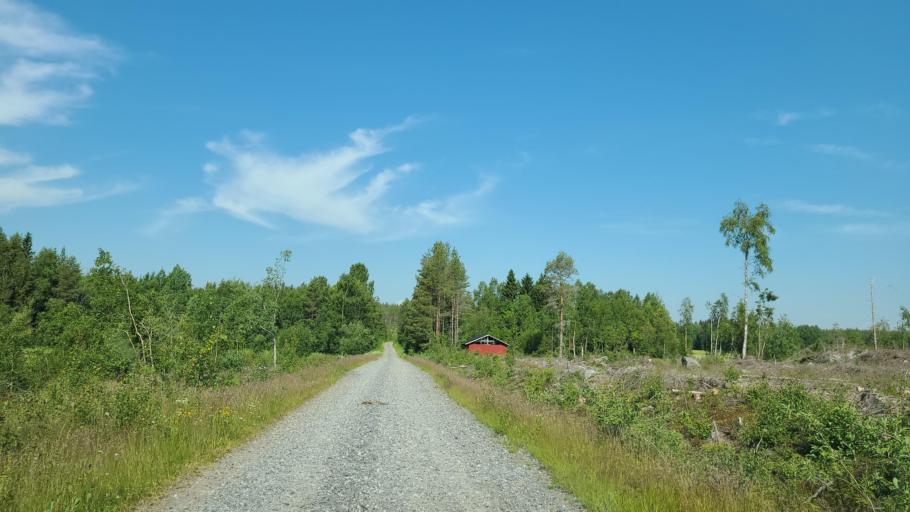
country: SE
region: Vaesterbotten
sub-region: Robertsfors Kommun
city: Robertsfors
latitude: 64.0889
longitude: 20.8386
